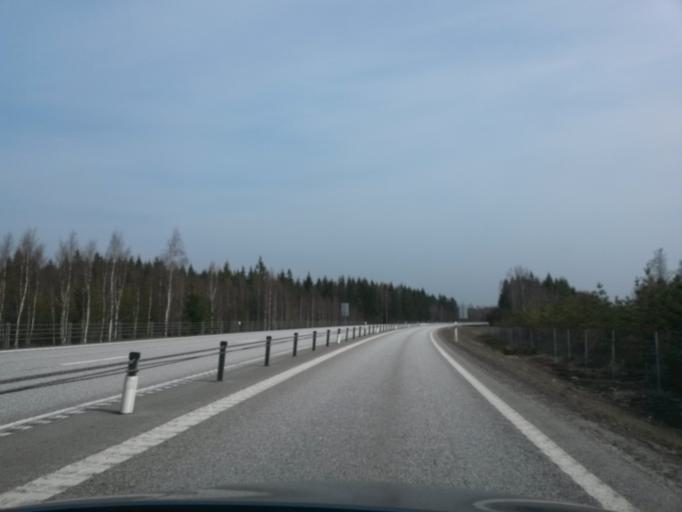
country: SE
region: Vaestra Goetaland
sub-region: Toreboda Kommun
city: Toereboda
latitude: 58.7959
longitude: 14.0244
